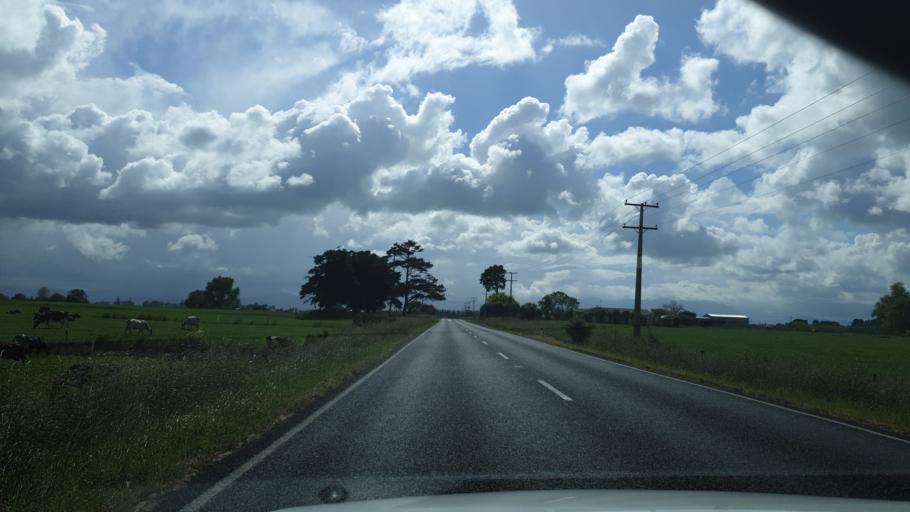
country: NZ
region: Waikato
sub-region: Hauraki District
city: Paeroa
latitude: -37.5136
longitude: 175.5095
